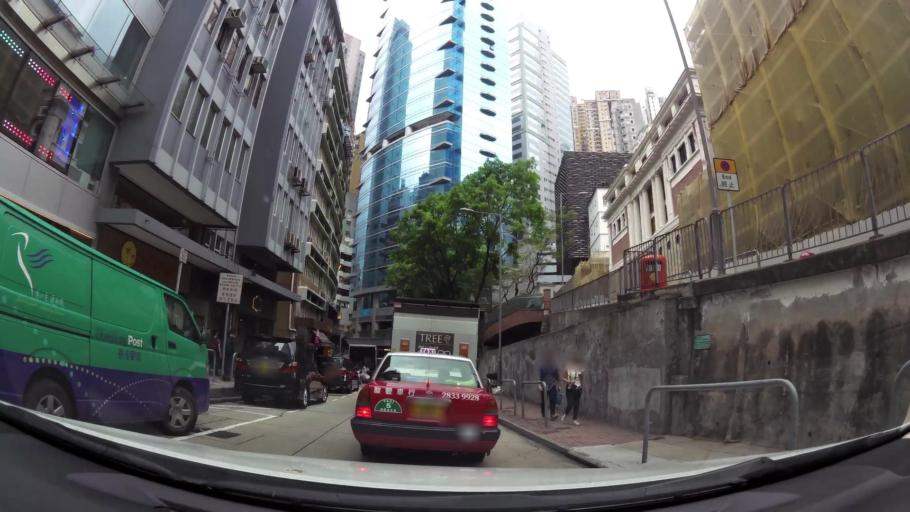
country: HK
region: Central and Western
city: Central
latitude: 22.2816
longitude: 114.1550
